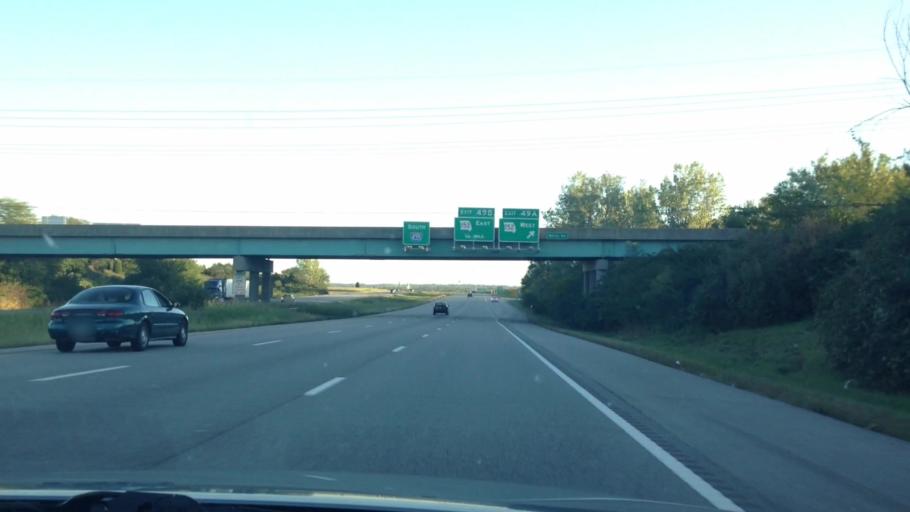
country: US
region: Missouri
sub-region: Clay County
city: Pleasant Valley
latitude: 39.2516
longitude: -94.5089
